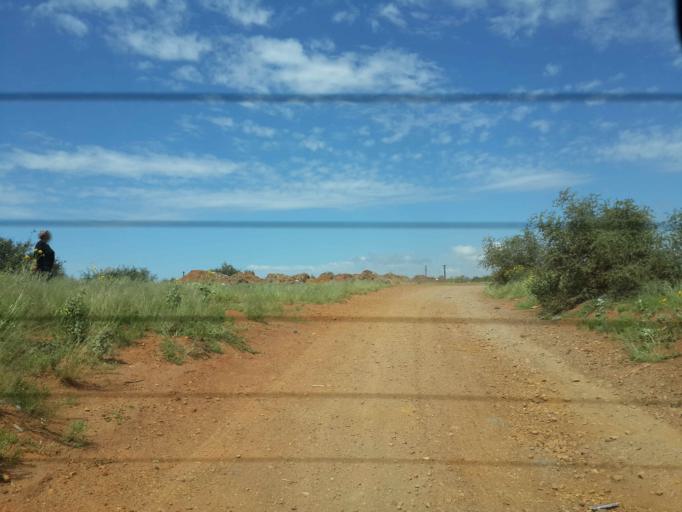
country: ZA
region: Northern Cape
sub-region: Siyanda District Municipality
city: Danielskuil
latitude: -28.1978
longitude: 23.5470
